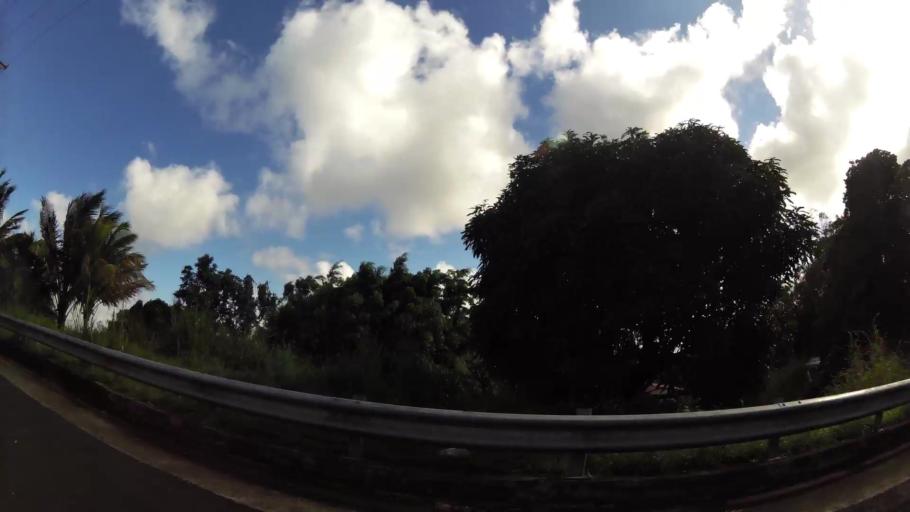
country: MQ
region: Martinique
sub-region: Martinique
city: Saint-Joseph
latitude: 14.6607
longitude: -61.0853
